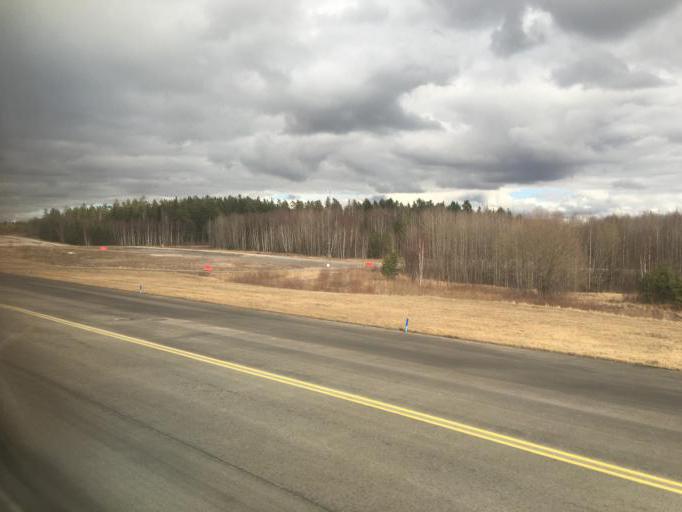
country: SE
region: Stockholm
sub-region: Sigtuna Kommun
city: Marsta
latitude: 59.6618
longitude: 17.9257
